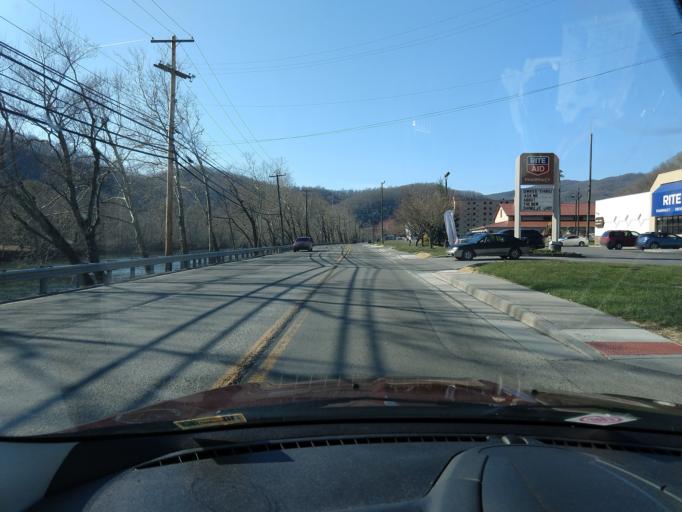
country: US
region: West Virginia
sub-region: Summers County
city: Hinton
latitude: 37.6567
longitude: -80.8883
